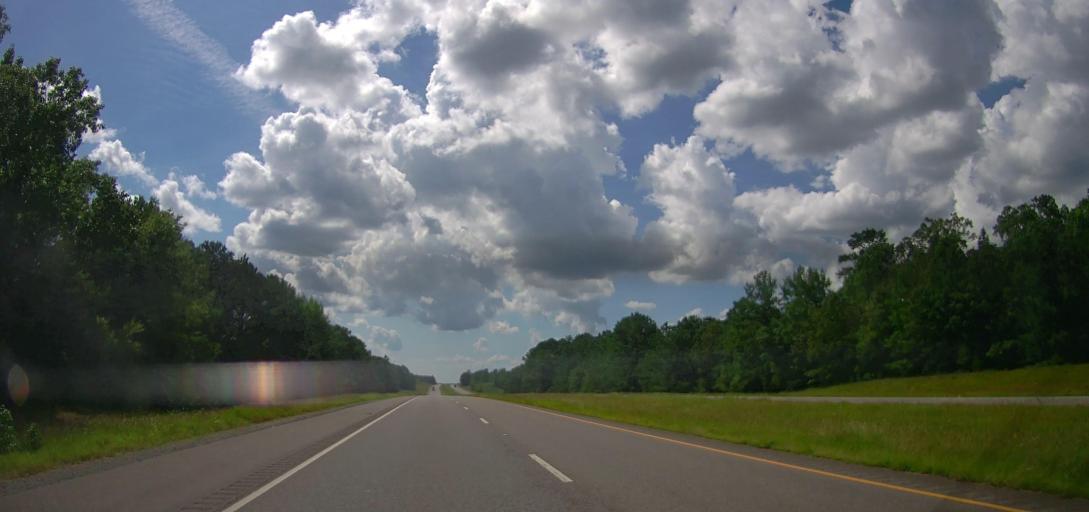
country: US
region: Alabama
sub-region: Pickens County
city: Reform
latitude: 33.3912
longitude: -88.0438
